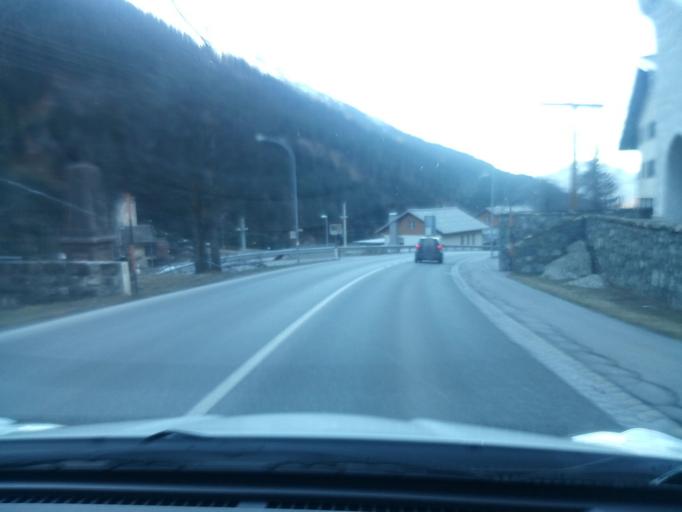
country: AT
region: Vorarlberg
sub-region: Politischer Bezirk Bludenz
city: Klosterle
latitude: 47.1322
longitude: 10.1235
